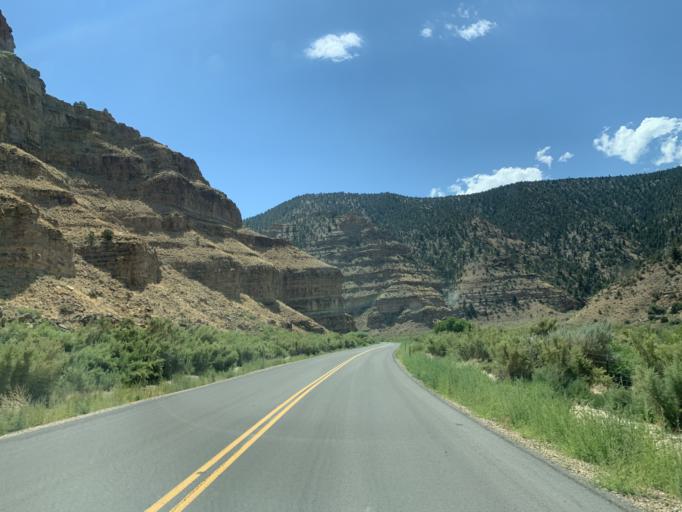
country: US
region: Utah
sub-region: Carbon County
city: East Carbon City
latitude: 39.8108
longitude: -110.2725
